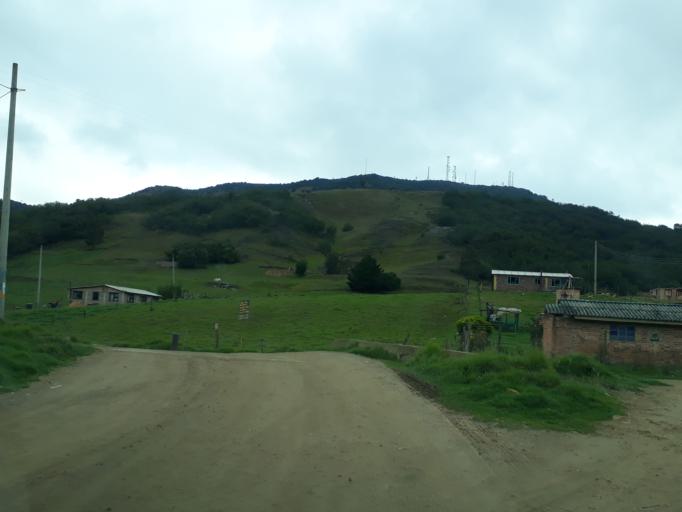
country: CO
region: Cundinamarca
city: Cucunuba
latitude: 5.2055
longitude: -73.7673
